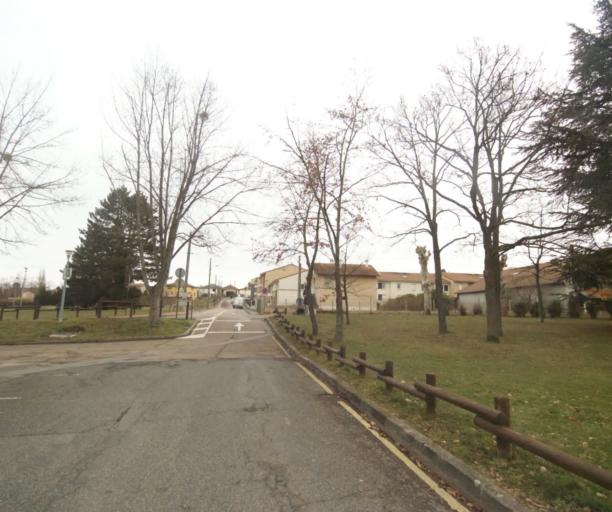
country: FR
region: Rhone-Alpes
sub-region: Departement de la Loire
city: Riorges
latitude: 46.0305
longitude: 4.0498
